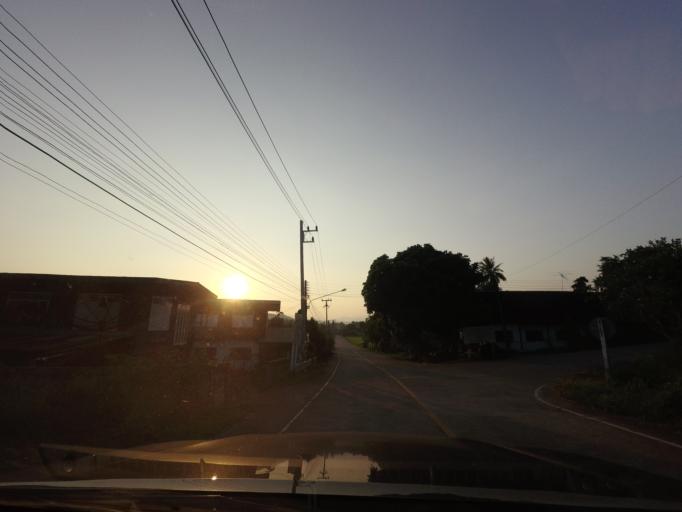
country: TH
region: Nan
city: Na Noi
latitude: 18.3100
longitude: 100.7337
